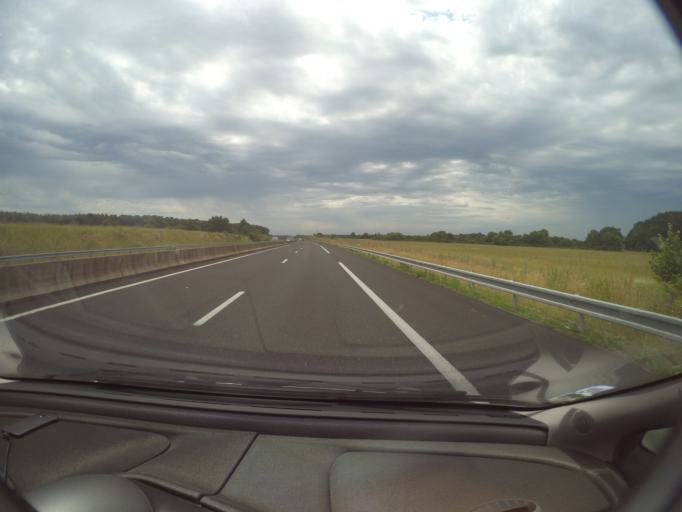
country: FR
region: Pays de la Loire
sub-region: Departement de Maine-et-Loire
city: Saint-Lambert-la-Potherie
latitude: 47.4866
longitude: -0.6586
